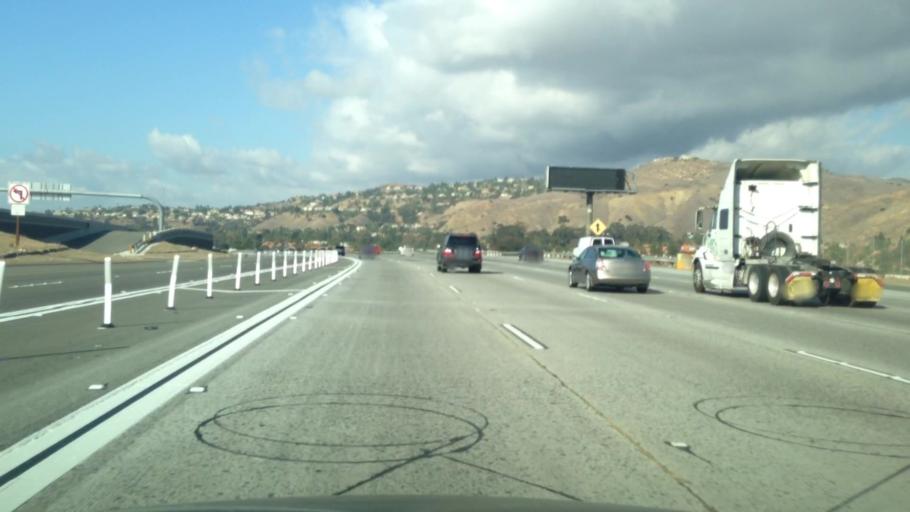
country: US
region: California
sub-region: San Bernardino County
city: Los Serranos
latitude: 33.8730
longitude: -117.6883
